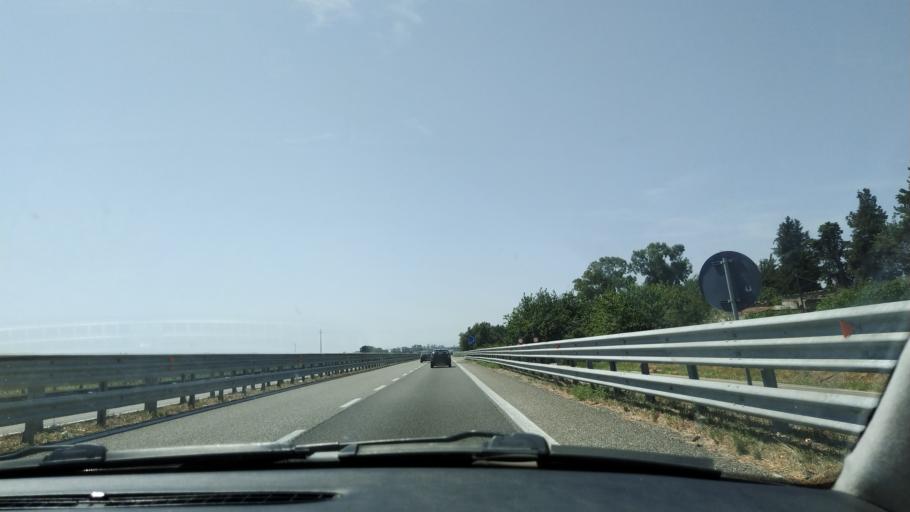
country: IT
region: Basilicate
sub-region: Provincia di Matera
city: Marconia
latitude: 40.3485
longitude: 16.7676
